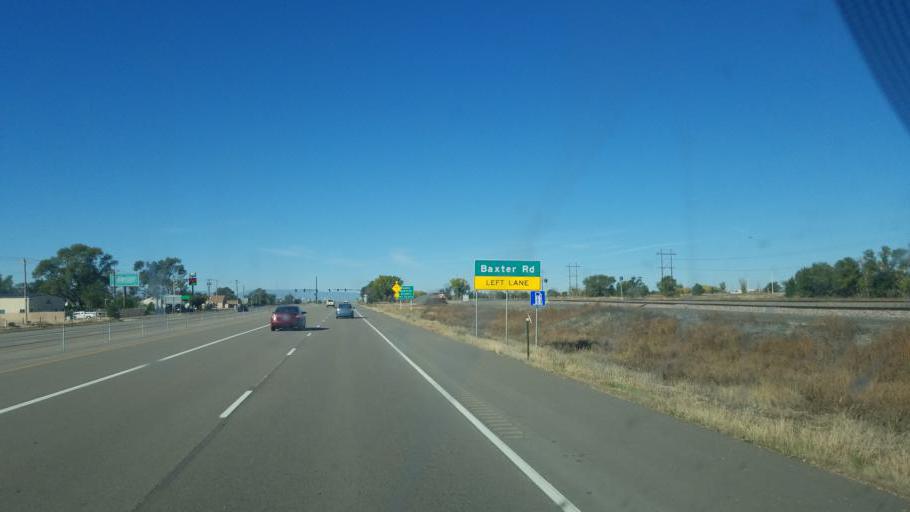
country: US
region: Colorado
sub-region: Pueblo County
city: Pueblo
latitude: 38.2753
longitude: -104.4930
